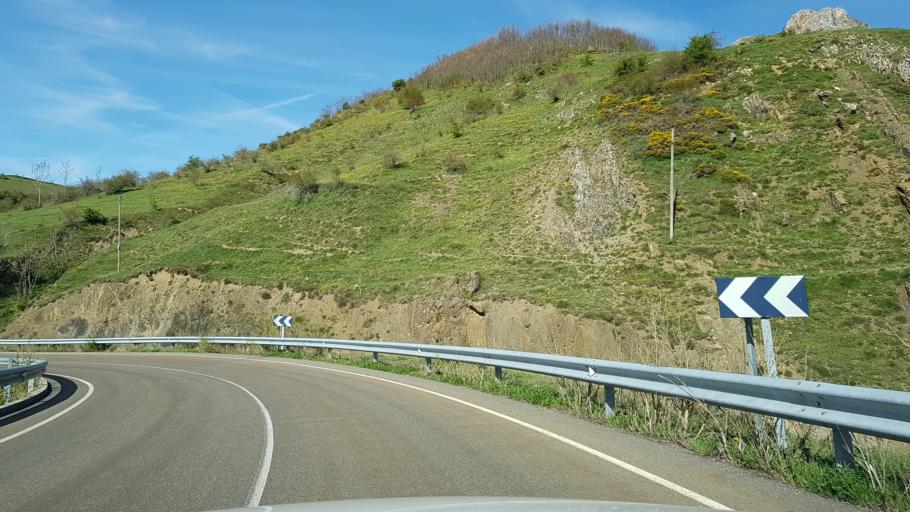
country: ES
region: Castille and Leon
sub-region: Provincia de Leon
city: Villamanin
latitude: 42.9521
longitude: -5.6369
